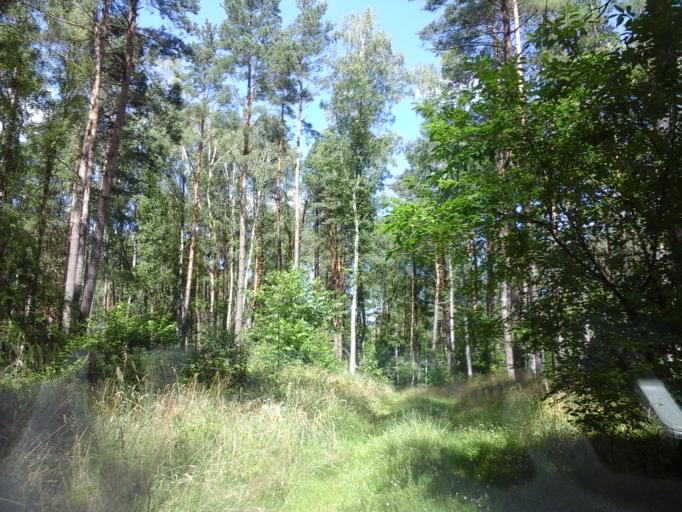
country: PL
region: West Pomeranian Voivodeship
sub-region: Powiat choszczenski
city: Recz
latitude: 53.2890
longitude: 15.6592
